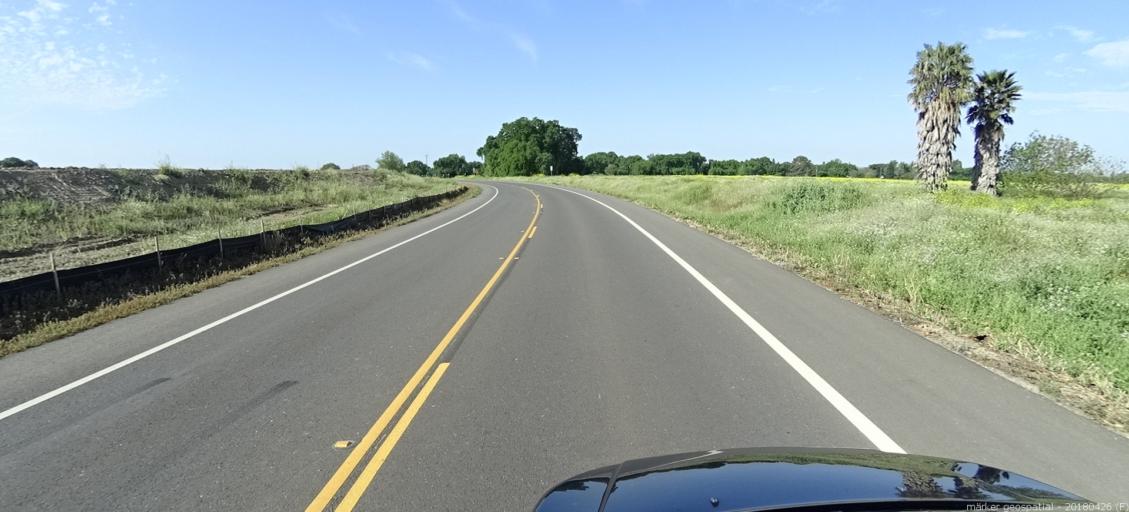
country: US
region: California
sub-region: Yolo County
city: West Sacramento
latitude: 38.5323
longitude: -121.5326
